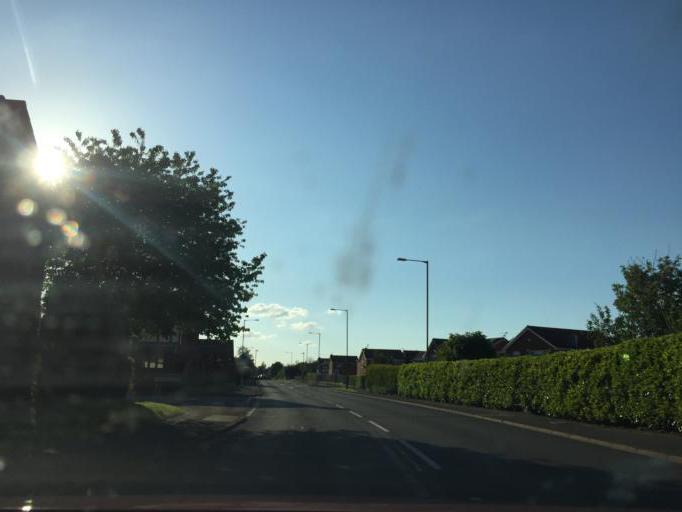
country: GB
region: England
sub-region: Warwickshire
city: Attleborough
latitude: 52.5111
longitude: -1.4401
